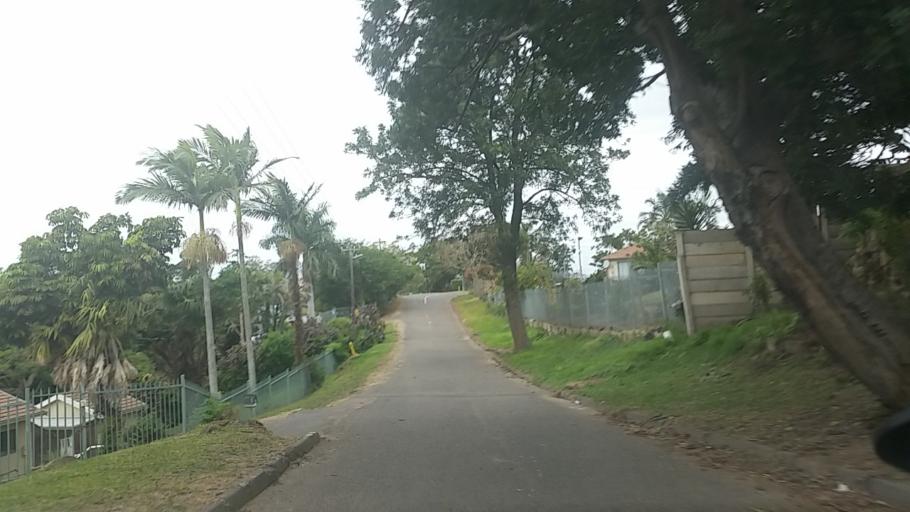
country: ZA
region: KwaZulu-Natal
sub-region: eThekwini Metropolitan Municipality
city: Berea
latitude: -29.8409
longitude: 30.9428
